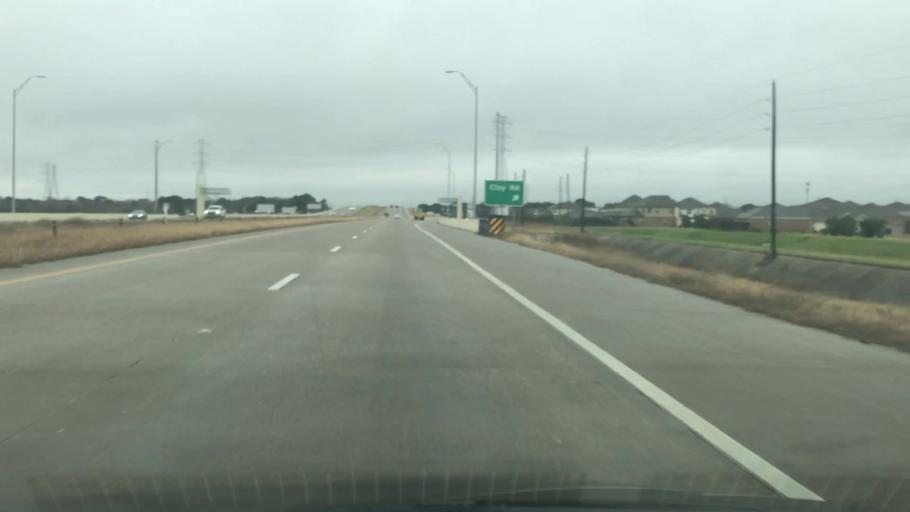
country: US
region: Texas
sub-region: Harris County
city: Katy
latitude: 29.8265
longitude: -95.7642
